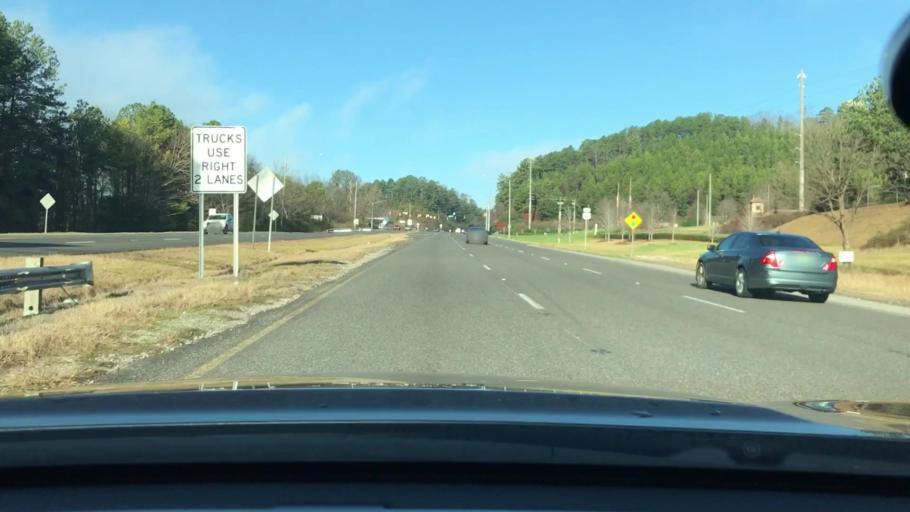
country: US
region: Alabama
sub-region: Jefferson County
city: Cahaba Heights
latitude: 33.4434
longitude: -86.7320
